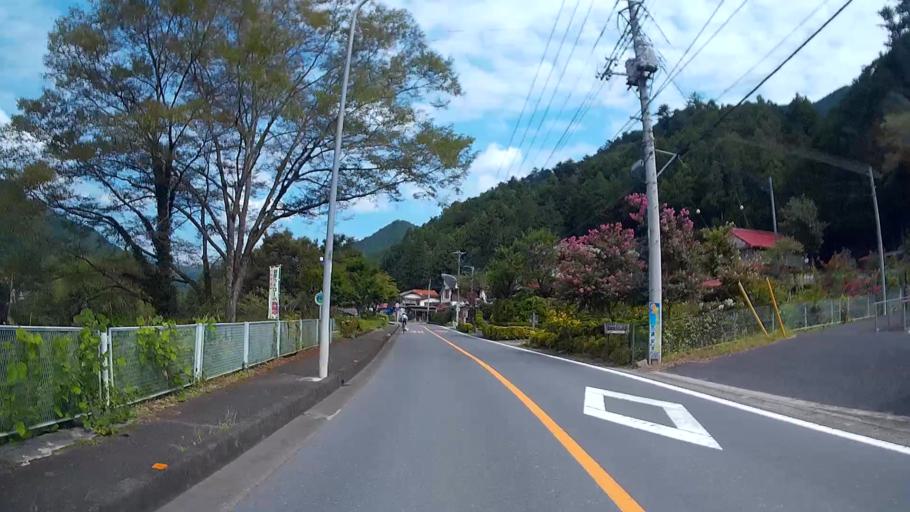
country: JP
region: Tokyo
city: Ome
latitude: 35.8781
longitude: 139.1858
